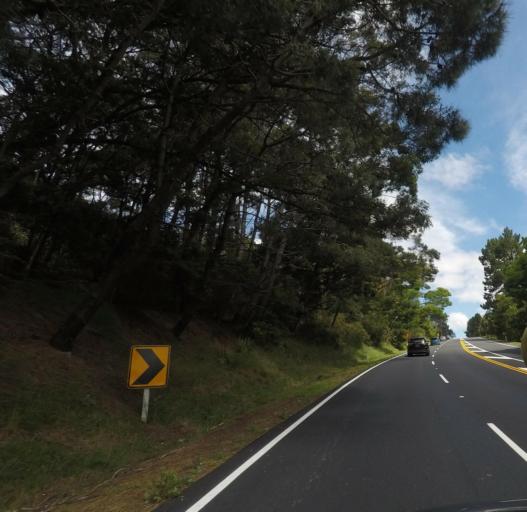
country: NZ
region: Auckland
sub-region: Auckland
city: Rothesay Bay
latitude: -36.6868
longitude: 174.7058
